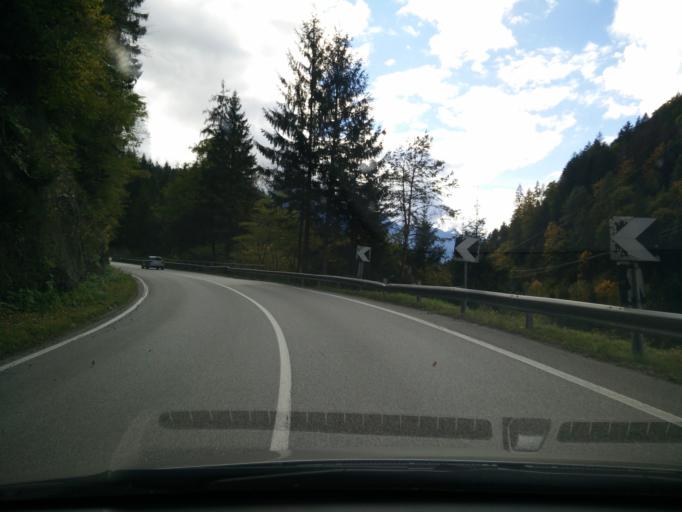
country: IT
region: Veneto
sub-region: Provincia di Belluno
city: Vigo di Cadore
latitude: 46.5244
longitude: 12.4667
